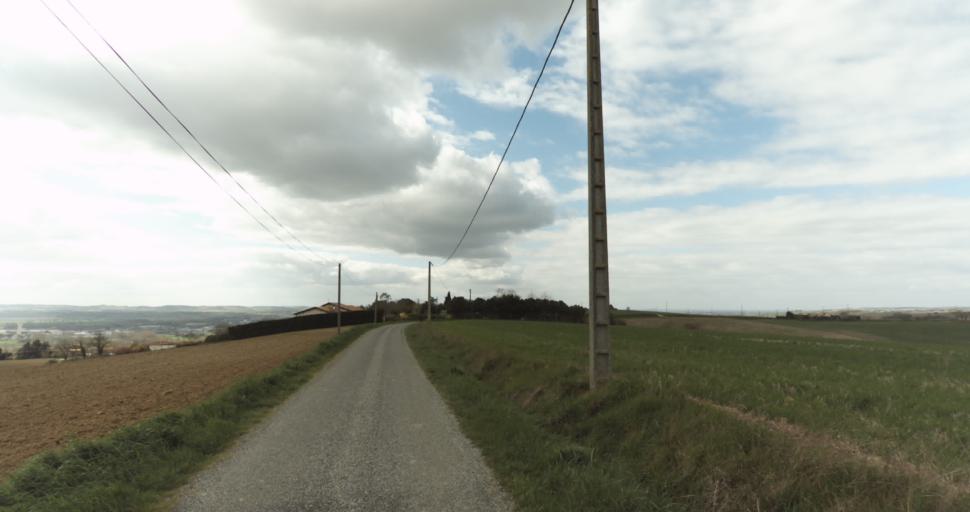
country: FR
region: Midi-Pyrenees
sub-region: Departement de la Haute-Garonne
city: Auterive
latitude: 43.3658
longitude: 1.4876
